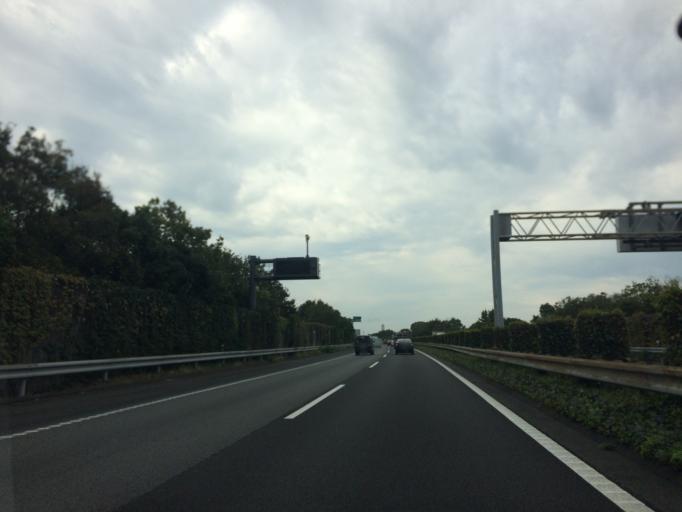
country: JP
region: Shizuoka
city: Fujieda
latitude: 34.8661
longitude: 138.2862
